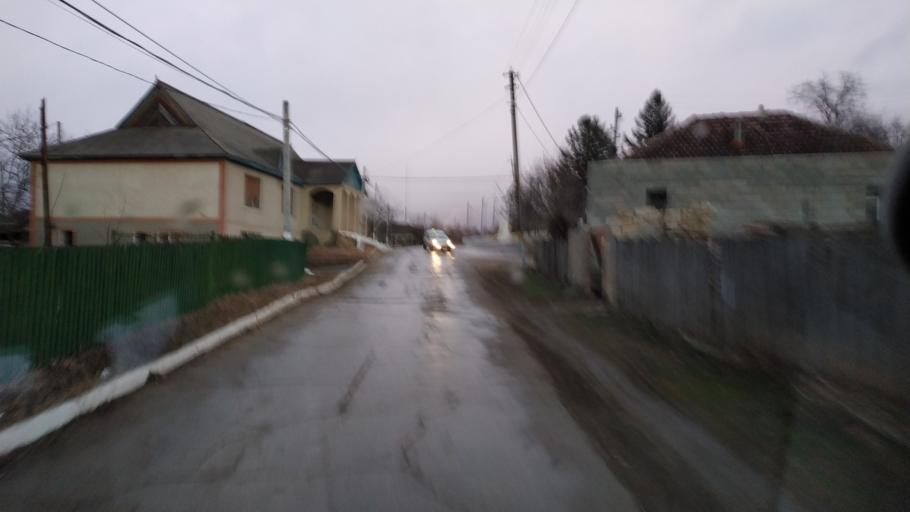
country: MD
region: Calarasi
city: Calarasi
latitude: 47.3738
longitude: 28.3194
